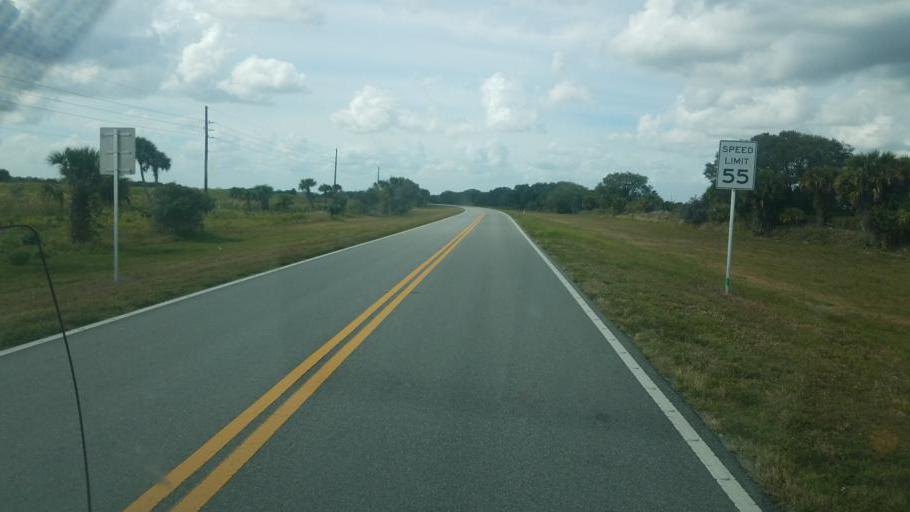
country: US
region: Florida
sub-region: Okeechobee County
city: Cypress Quarters
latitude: 27.4495
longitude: -80.6853
